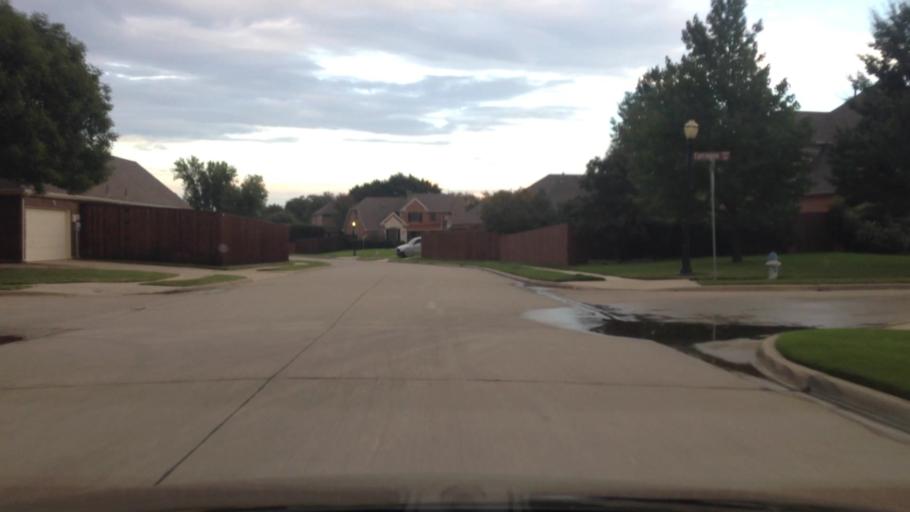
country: US
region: Texas
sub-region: Denton County
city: Flower Mound
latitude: 33.0048
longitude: -97.0426
